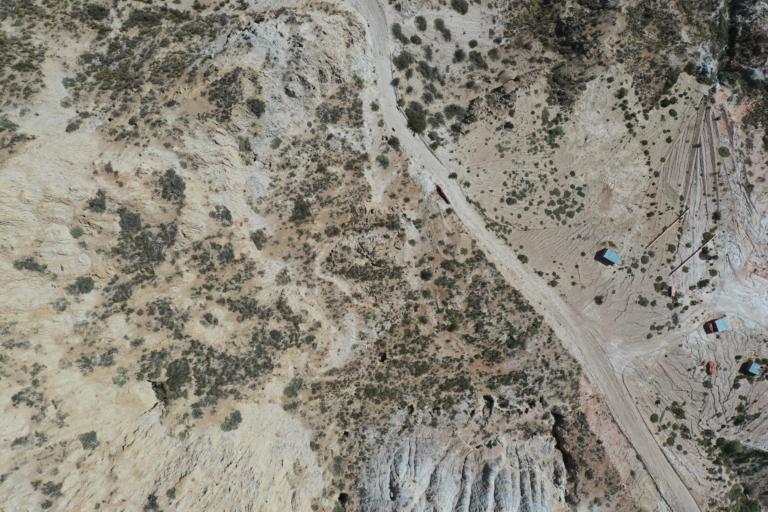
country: BO
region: La Paz
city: La Paz
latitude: -16.5540
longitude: -68.1226
